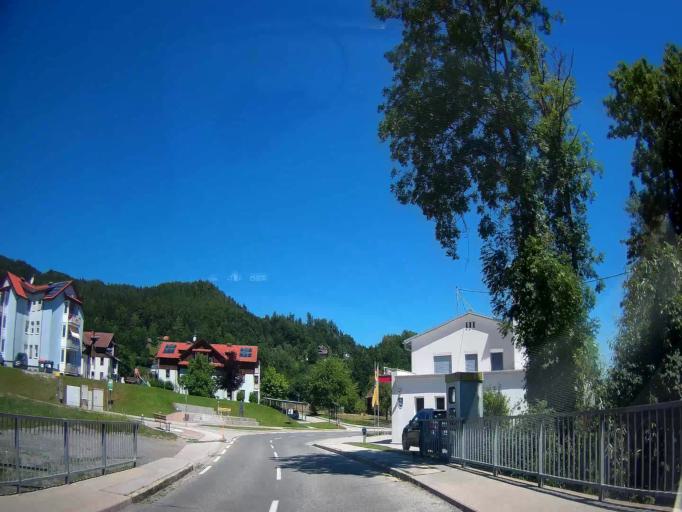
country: AT
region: Carinthia
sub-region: Politischer Bezirk Klagenfurt Land
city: Maria Worth
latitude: 46.6027
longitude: 14.1732
